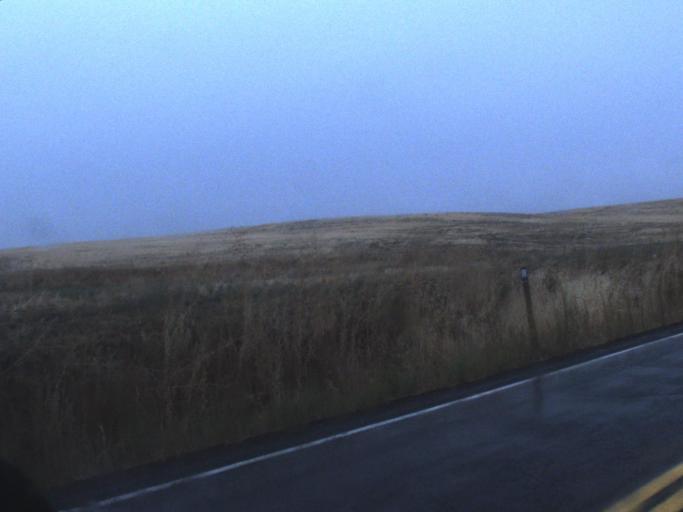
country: US
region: Washington
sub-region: Lincoln County
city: Davenport
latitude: 47.3479
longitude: -118.0875
